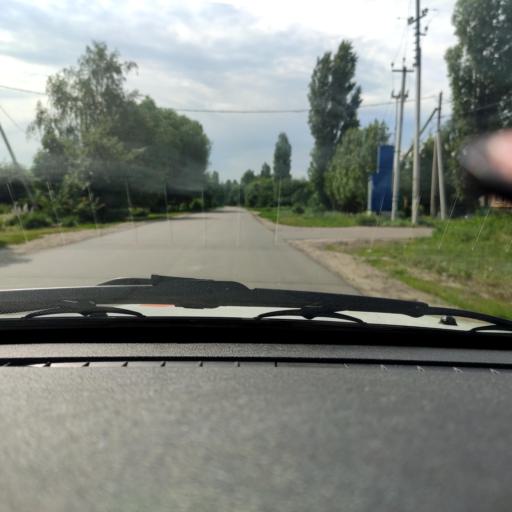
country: RU
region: Voronezj
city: Novaya Usman'
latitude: 51.6165
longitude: 39.3989
